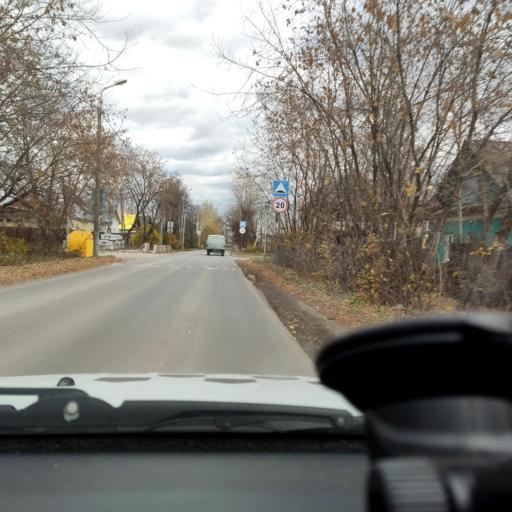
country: RU
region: Perm
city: Perm
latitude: 57.9935
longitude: 56.3088
